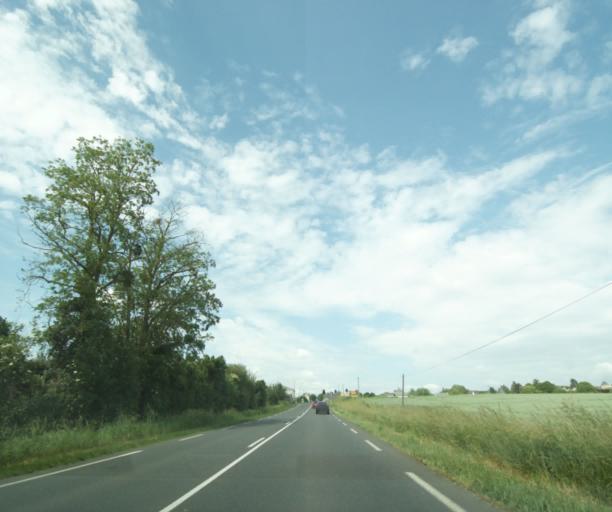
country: FR
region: Pays de la Loire
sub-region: Departement de Maine-et-Loire
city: Distre
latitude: 47.1917
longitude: -0.1275
